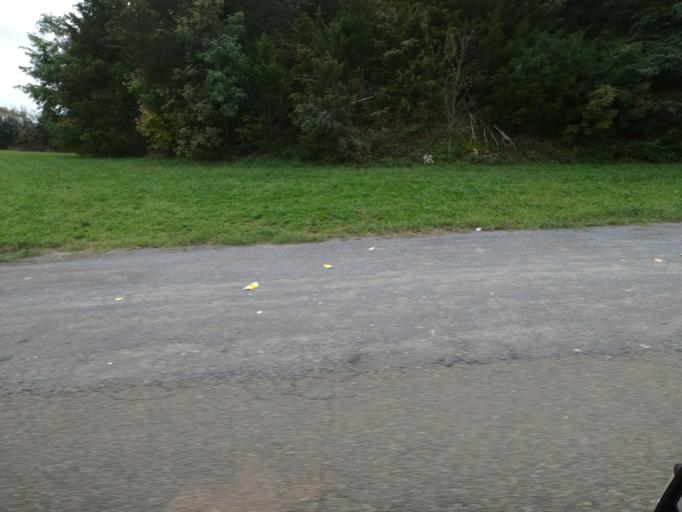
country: US
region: Tennessee
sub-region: Jefferson County
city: White Pine
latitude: 36.1381
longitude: -83.2787
